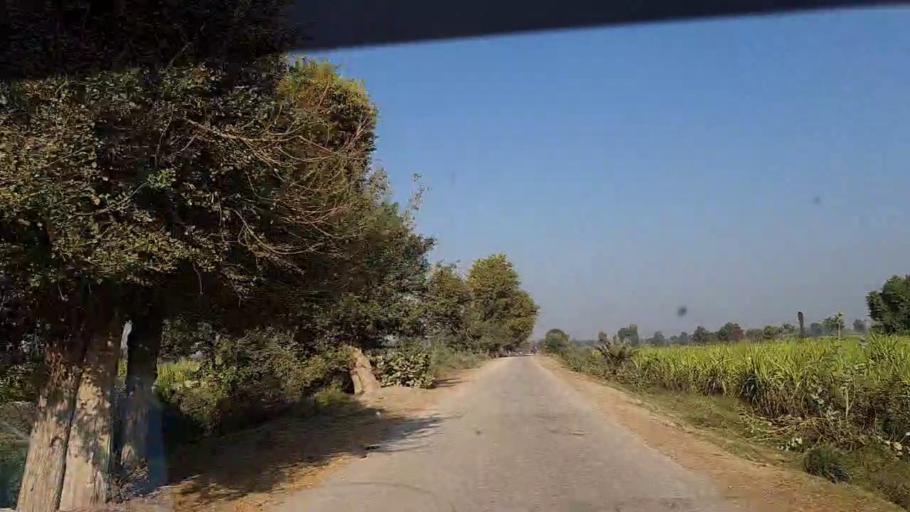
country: PK
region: Sindh
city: Sobhadero
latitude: 27.2482
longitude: 68.3268
